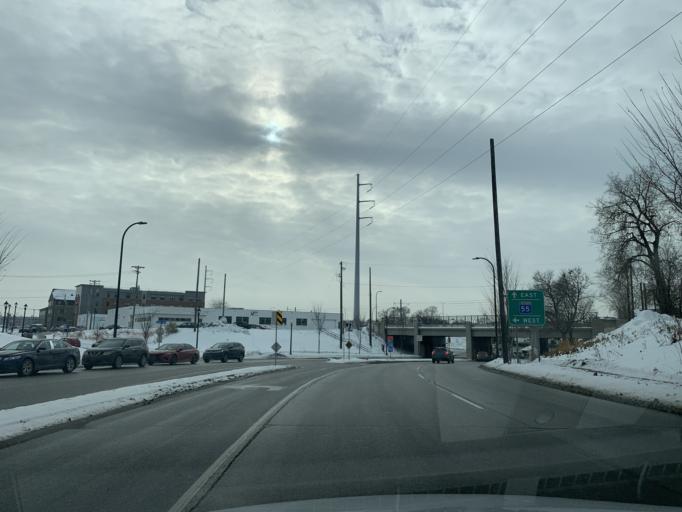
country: US
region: Minnesota
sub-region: Hennepin County
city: Minneapolis
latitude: 44.9619
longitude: -93.2452
